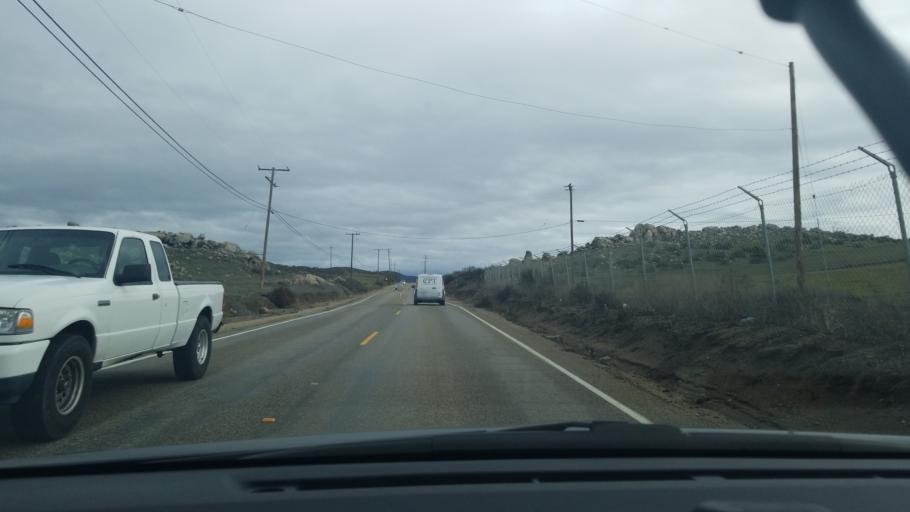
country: US
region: California
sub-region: Riverside County
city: Winchester
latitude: 33.6417
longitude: -117.0962
